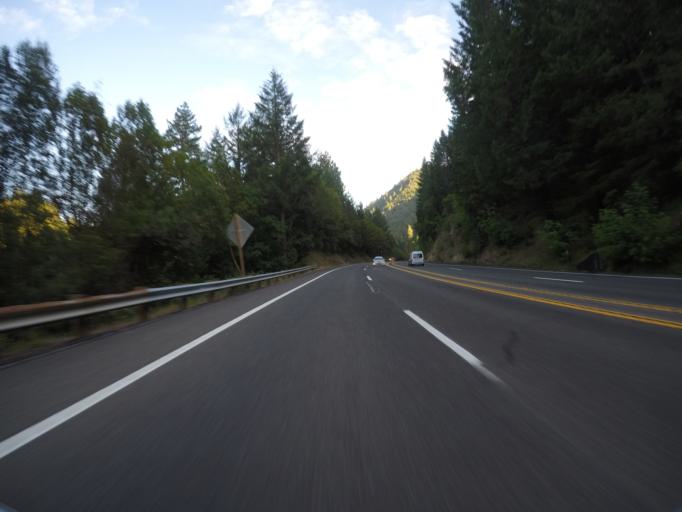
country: US
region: California
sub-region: Mendocino County
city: Brooktrails
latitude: 39.5405
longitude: -123.4182
